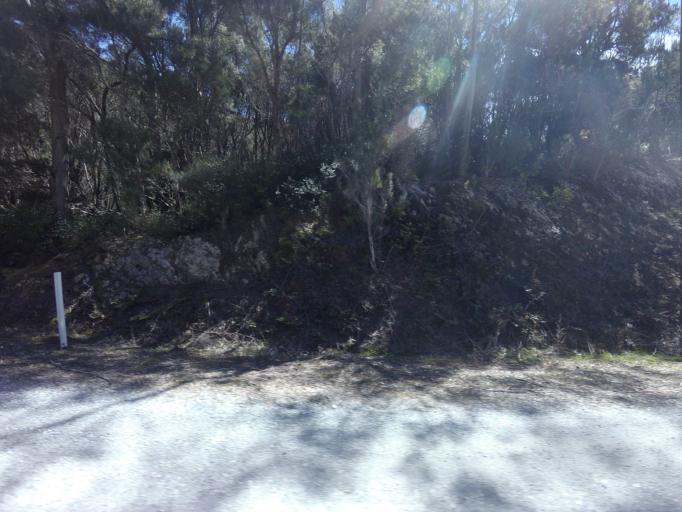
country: AU
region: Tasmania
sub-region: West Coast
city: Queenstown
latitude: -42.7657
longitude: 145.9858
